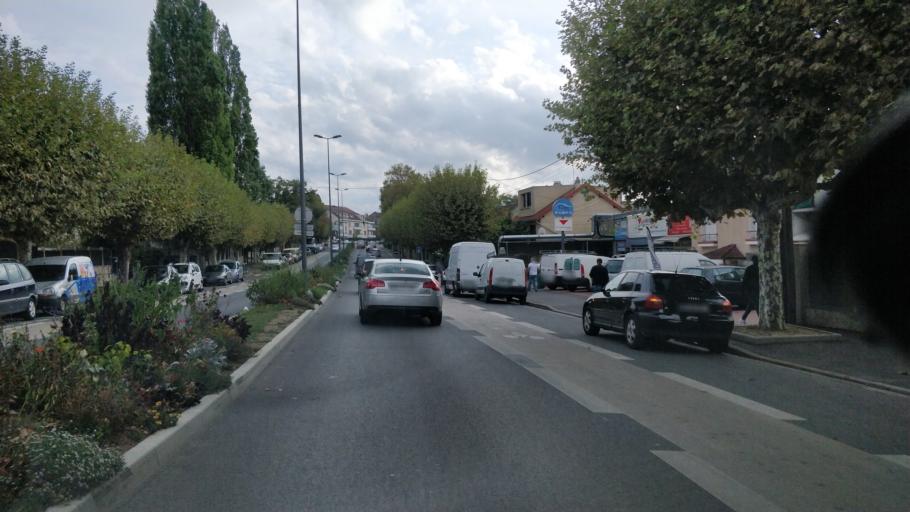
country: FR
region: Ile-de-France
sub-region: Departement de Seine-Saint-Denis
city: Clichy-sous-Bois
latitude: 48.9010
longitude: 2.5468
